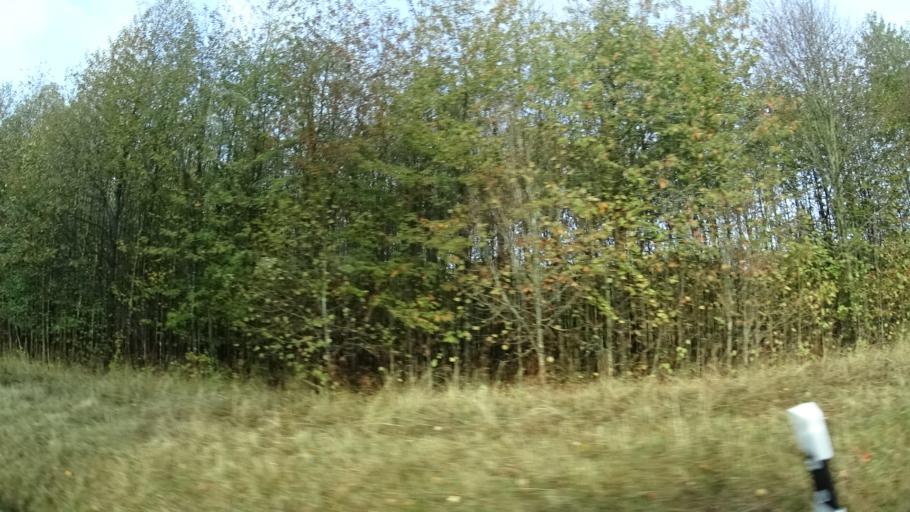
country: DE
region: Hesse
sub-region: Regierungsbezirk Giessen
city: Grebenhain
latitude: 50.4934
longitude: 9.3978
